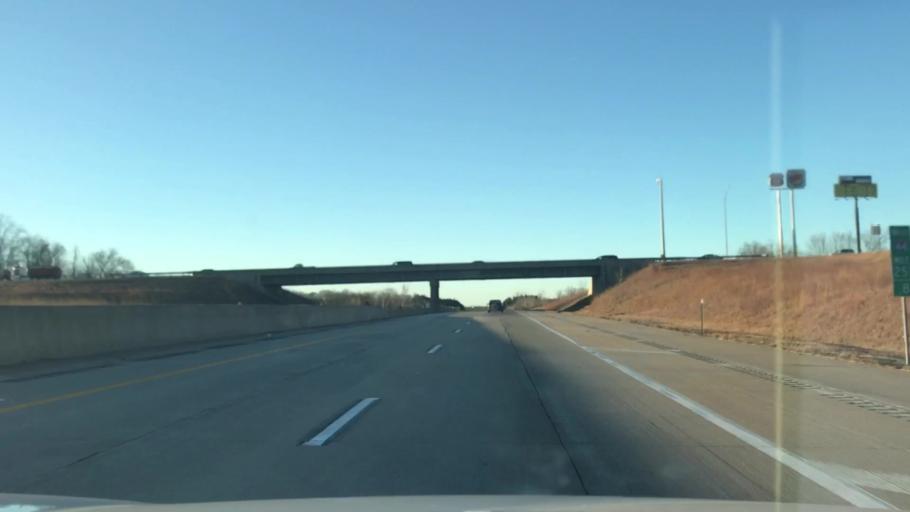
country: US
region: Missouri
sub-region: Franklin County
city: Gray Summit
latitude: 38.4756
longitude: -90.8498
